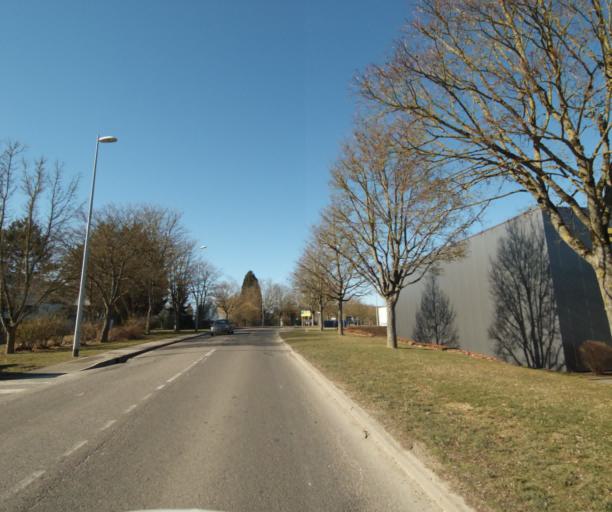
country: FR
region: Lorraine
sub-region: Departement de Meurthe-et-Moselle
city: Richardmenil
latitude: 48.6127
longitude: 6.1842
